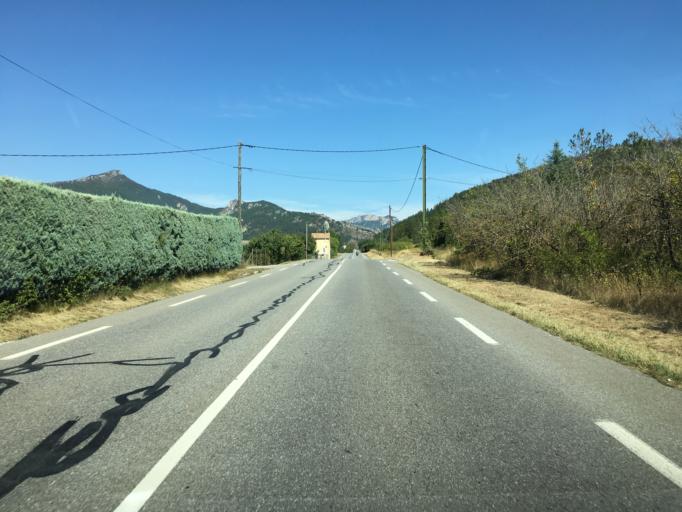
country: FR
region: Provence-Alpes-Cote d'Azur
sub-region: Departement des Hautes-Alpes
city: Serres
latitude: 44.4113
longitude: 5.7259
